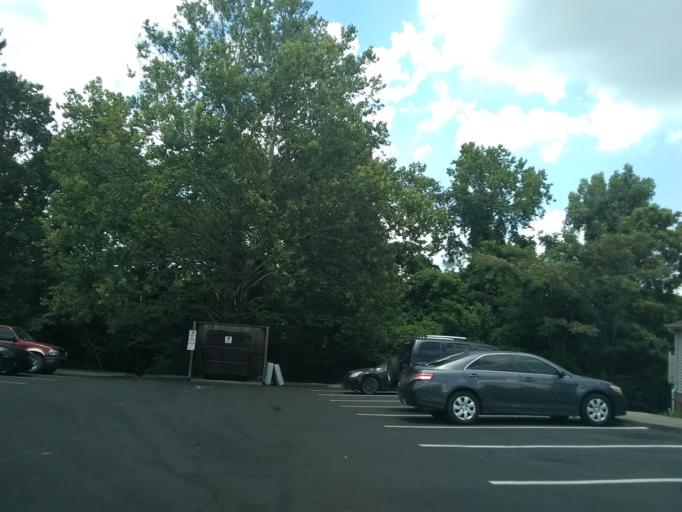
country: US
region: Tennessee
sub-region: Davidson County
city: Lakewood
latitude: 36.1514
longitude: -86.6823
